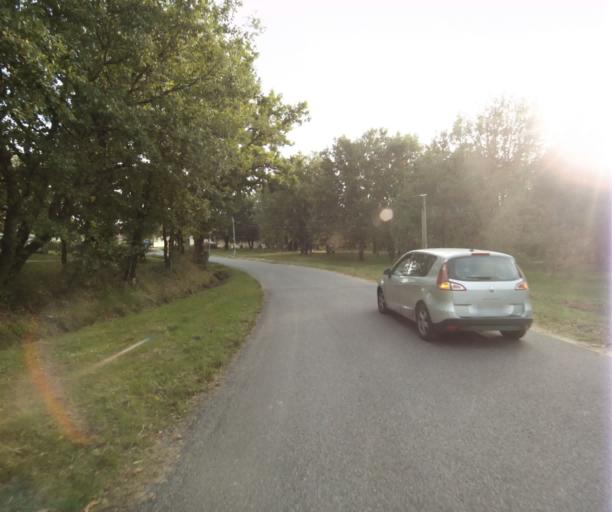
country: FR
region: Midi-Pyrenees
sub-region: Departement du Tarn-et-Garonne
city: Campsas
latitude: 43.8931
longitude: 1.3257
